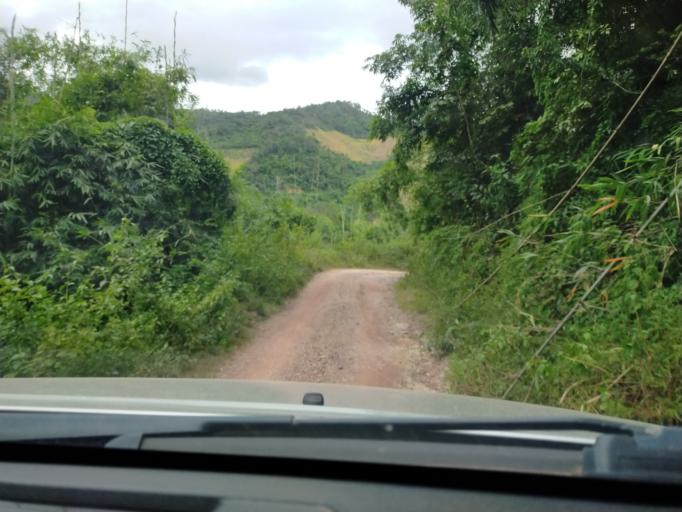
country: TH
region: Nan
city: Chaloem Phra Kiat
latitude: 19.7964
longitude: 101.3629
